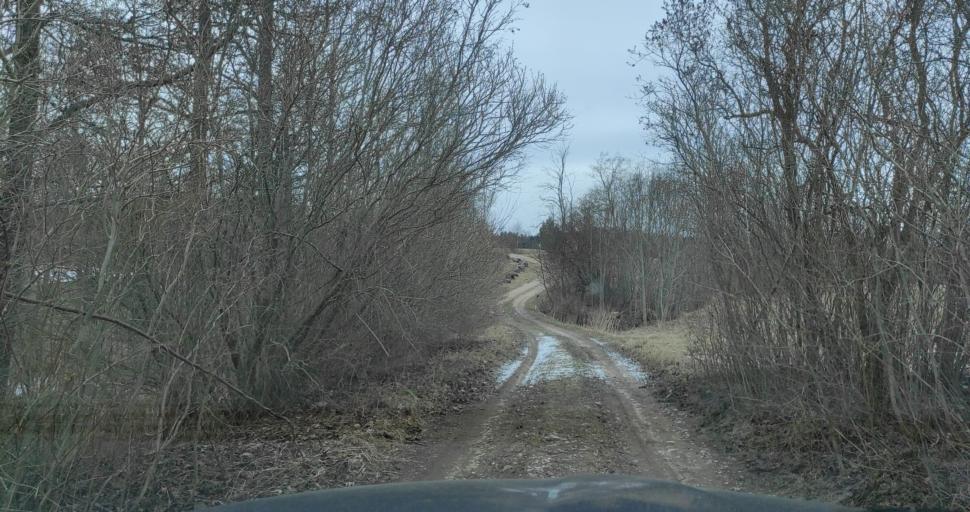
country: LV
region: Tukuma Rajons
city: Tukums
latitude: 57.0975
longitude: 23.0913
